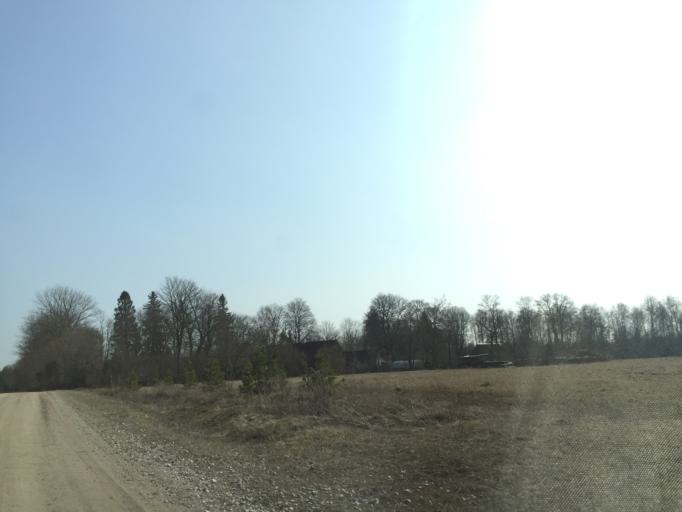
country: EE
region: Saare
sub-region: Kuressaare linn
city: Kuressaare
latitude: 58.3800
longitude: 22.7197
